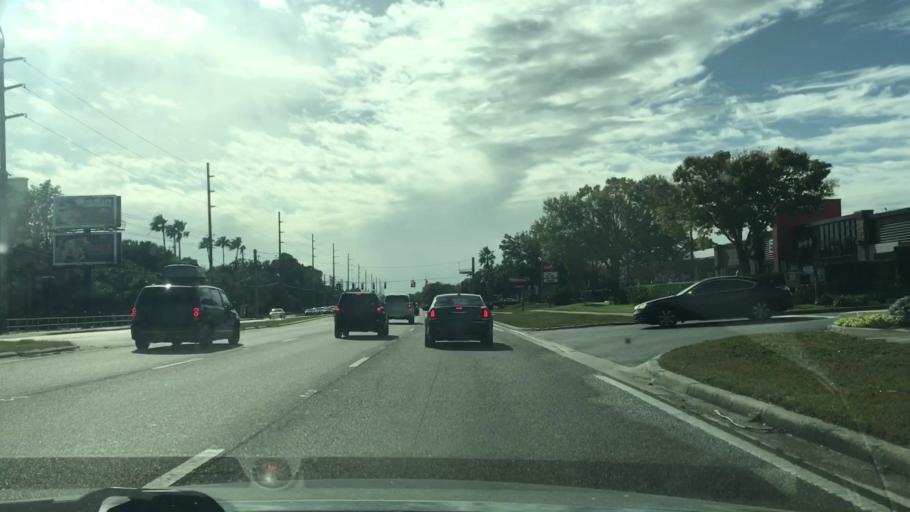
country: US
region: Florida
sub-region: Osceola County
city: Celebration
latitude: 28.3721
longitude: -81.5037
